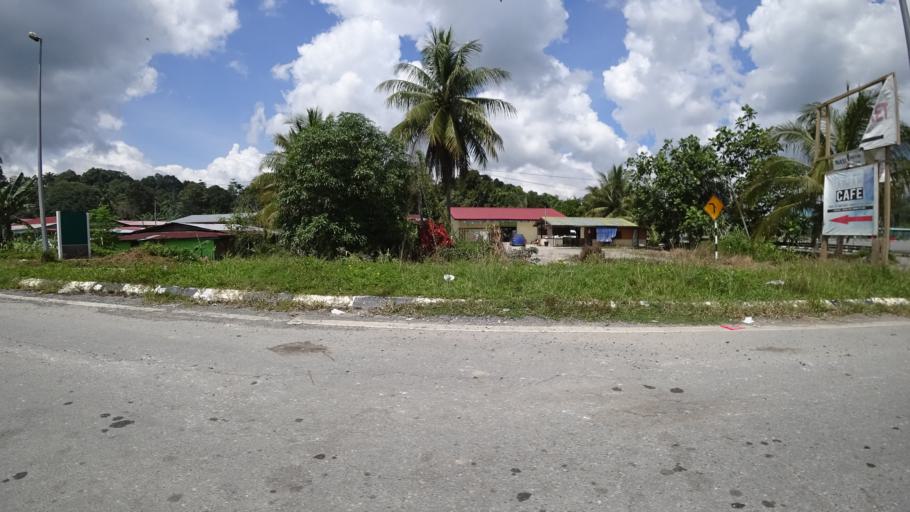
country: BN
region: Tutong
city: Tutong
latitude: 4.7366
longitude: 114.8109
